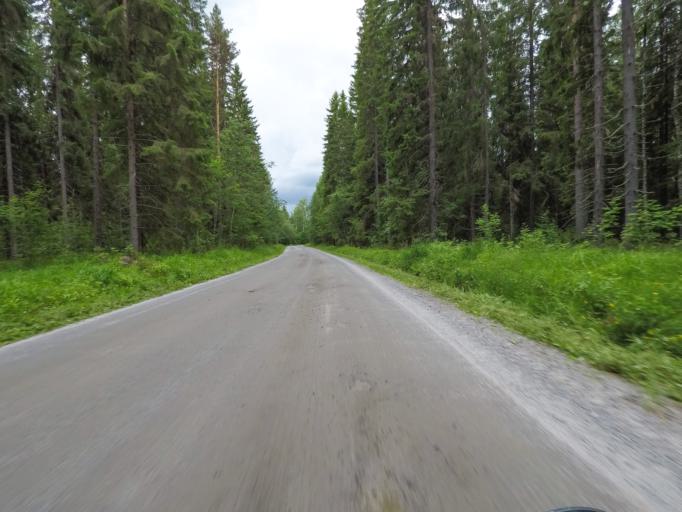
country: FI
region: Central Finland
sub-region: Jyvaeskylae
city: Hankasalmi
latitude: 62.4212
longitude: 26.6465
